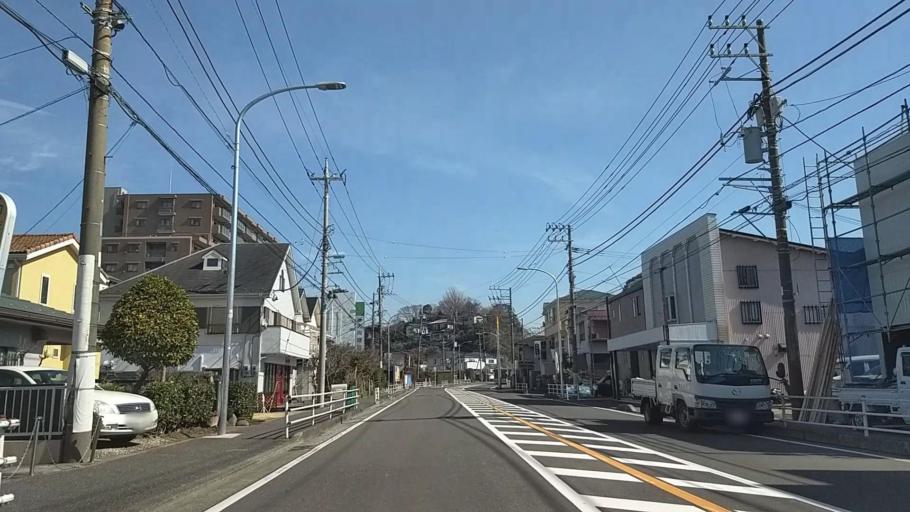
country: JP
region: Kanagawa
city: Kamakura
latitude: 35.3599
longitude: 139.5363
